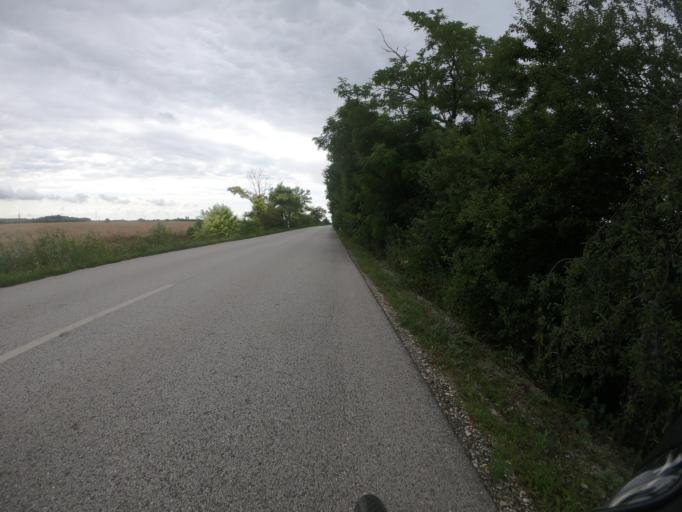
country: HU
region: Heves
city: Poroszlo
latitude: 47.6972
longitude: 20.7224
